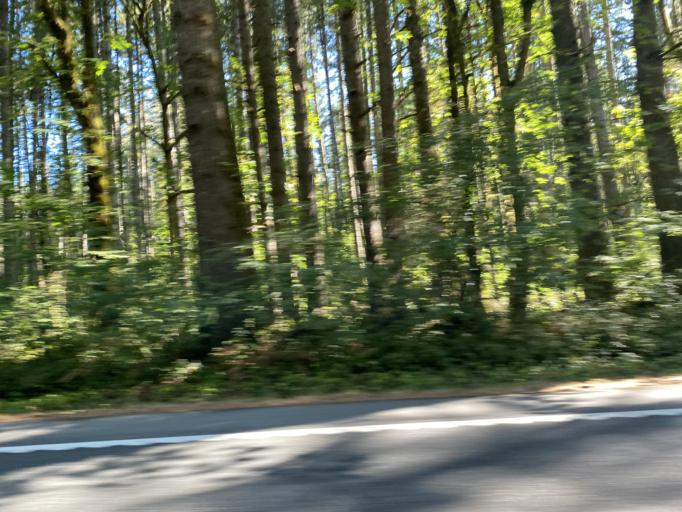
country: US
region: Washington
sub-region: Thurston County
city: Rainier
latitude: 46.9299
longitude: -122.7545
